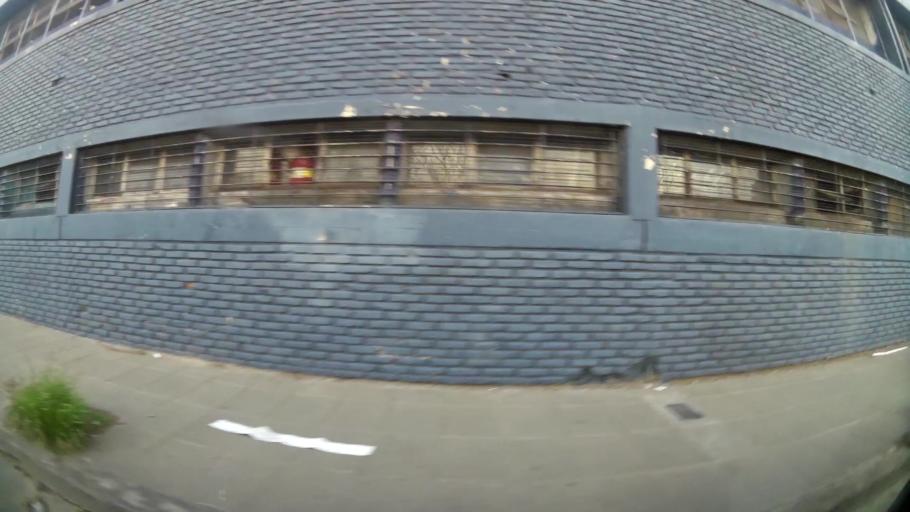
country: AR
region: Cordoba
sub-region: Departamento de Capital
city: Cordoba
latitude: -31.3955
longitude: -64.2021
